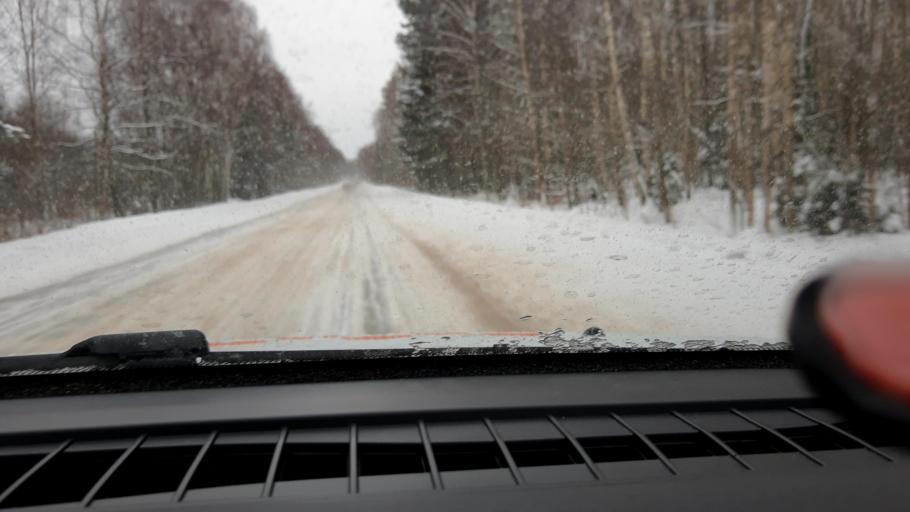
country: RU
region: Nizjnij Novgorod
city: Pamyat' Parizhskoy Kommuny
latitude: 56.2586
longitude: 44.4562
